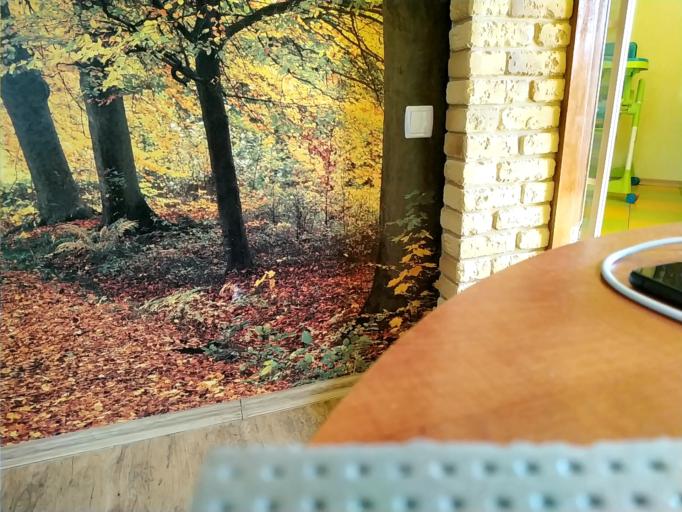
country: RU
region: Tverskaya
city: Kalashnikovo
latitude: 57.3507
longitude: 35.1800
